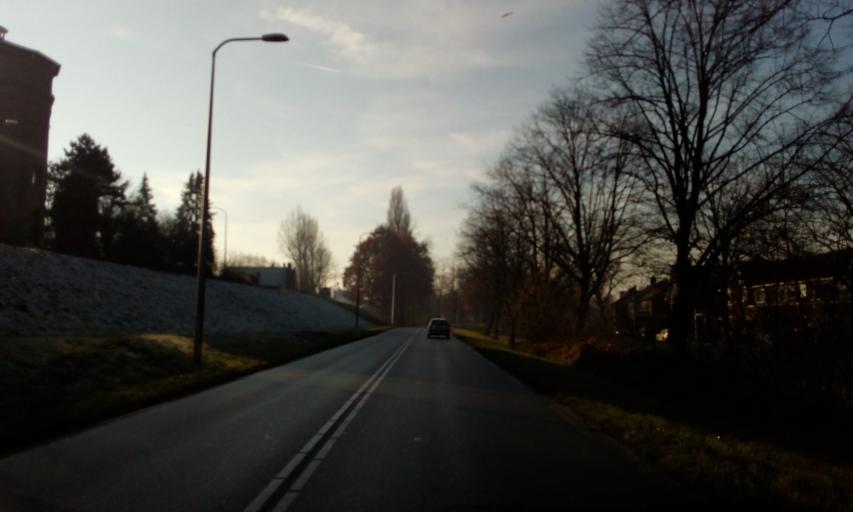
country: NL
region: South Holland
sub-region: Gemeente Gouda
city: Gouda
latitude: 52.0023
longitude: 4.7047
